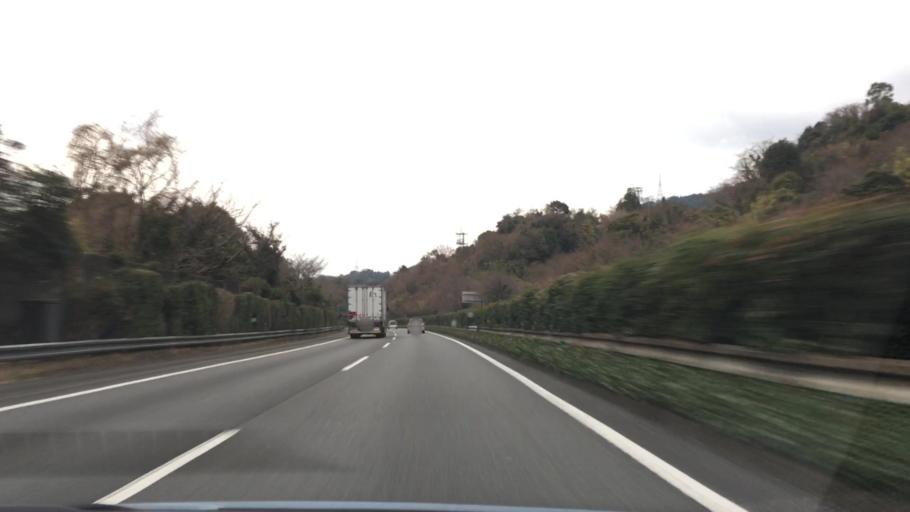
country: JP
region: Shizuoka
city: Fujinomiya
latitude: 35.1489
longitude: 138.6151
